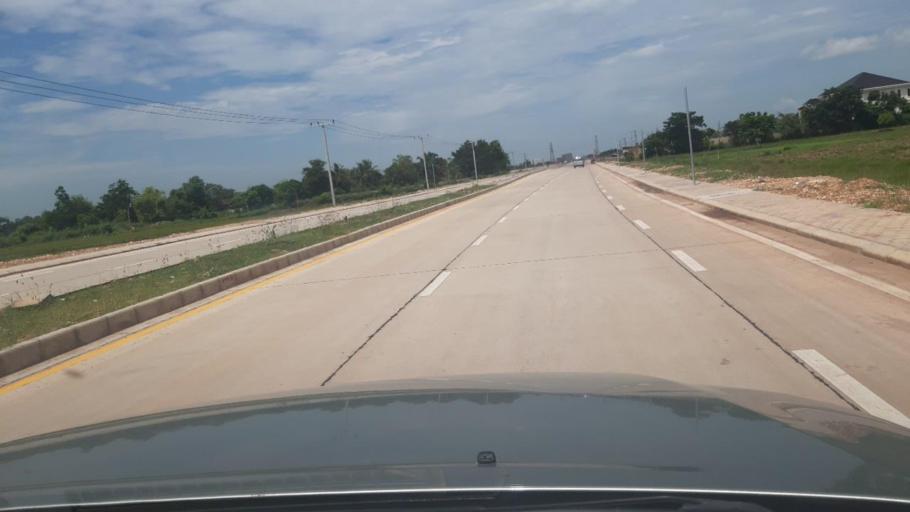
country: LA
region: Vientiane
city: Vientiane
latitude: 18.0290
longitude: 102.6070
